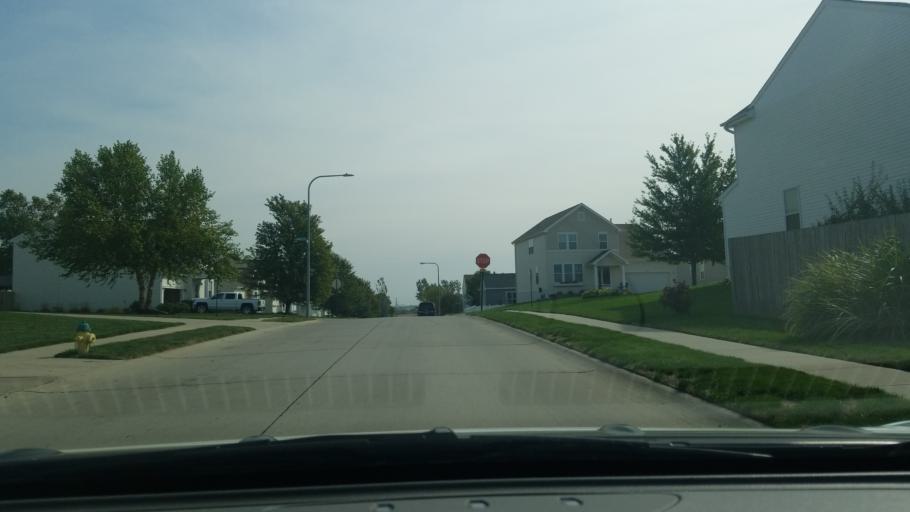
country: US
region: Nebraska
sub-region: Sarpy County
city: Papillion
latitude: 41.1286
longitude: -96.0561
